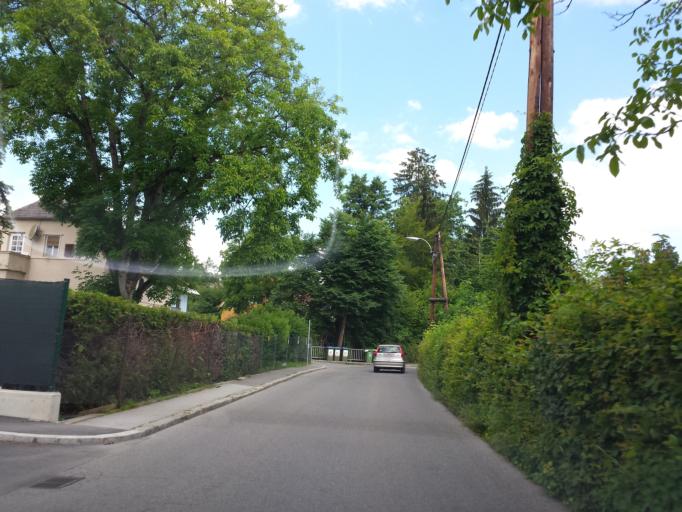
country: AT
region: Styria
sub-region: Graz Stadt
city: Graz
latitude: 47.0915
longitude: 15.4574
